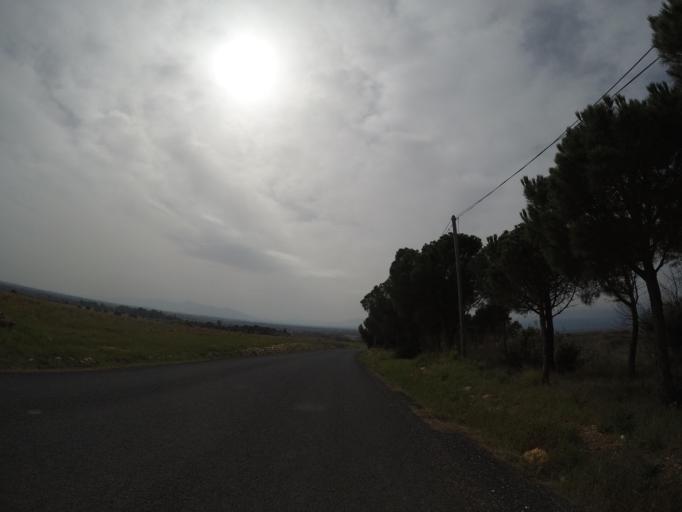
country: FR
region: Languedoc-Roussillon
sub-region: Departement des Pyrenees-Orientales
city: Pezilla-la-Riviere
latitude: 42.7105
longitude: 2.7591
